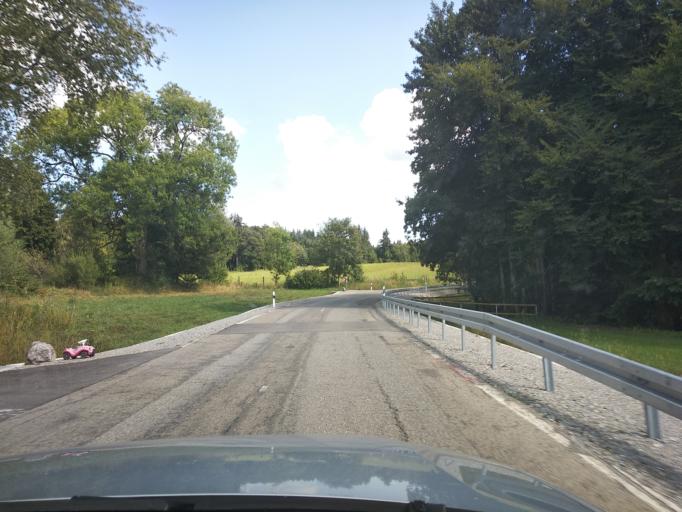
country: DE
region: Baden-Wuerttemberg
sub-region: Tuebingen Region
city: Leutkirch im Allgau
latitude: 47.8778
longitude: 9.9924
